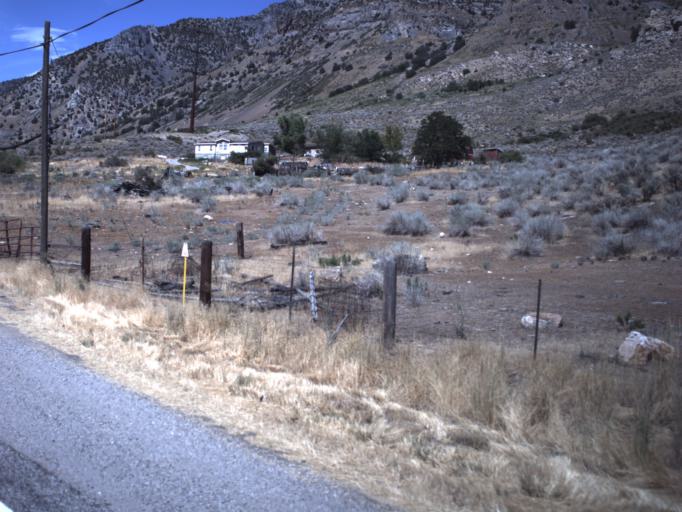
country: US
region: Utah
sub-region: Box Elder County
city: Brigham City
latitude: 41.5563
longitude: -112.0204
